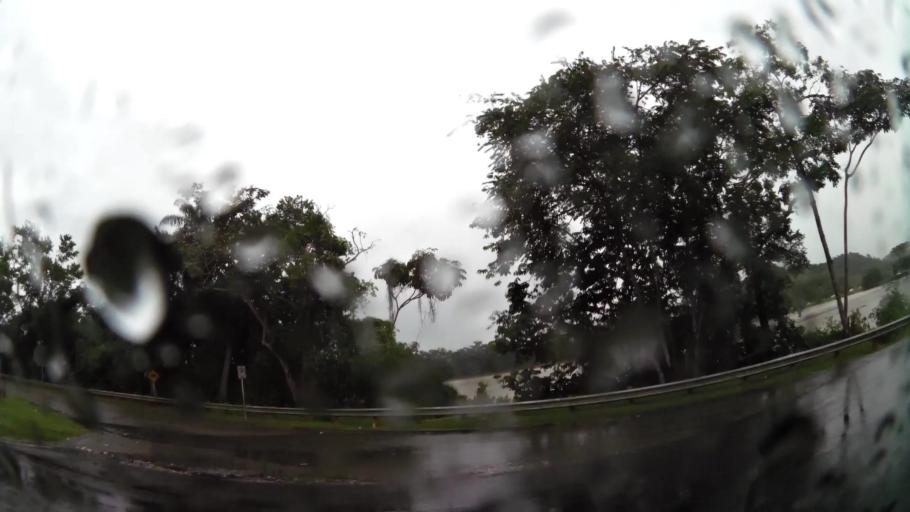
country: PA
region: Panama
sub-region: Distrito de Panama
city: Paraiso
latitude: 9.0111
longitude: -79.5956
